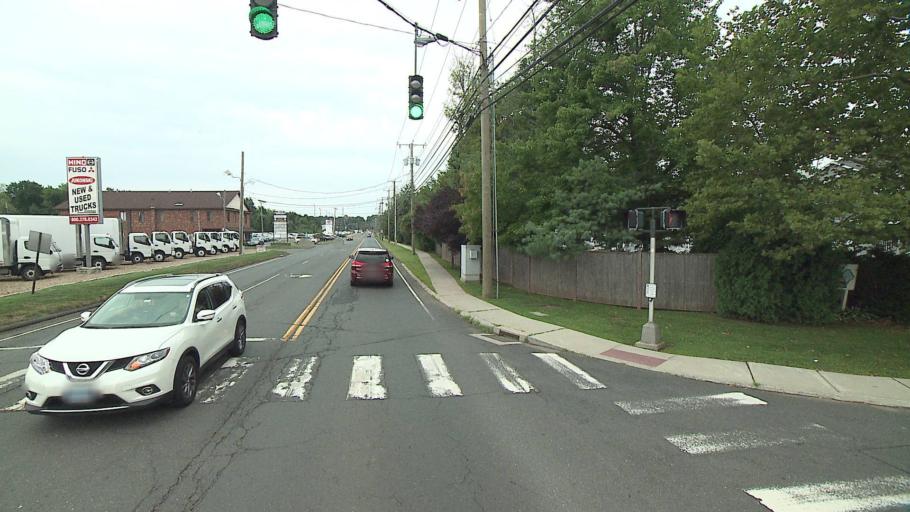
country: US
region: Connecticut
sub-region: Middlesex County
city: Middletown
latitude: 41.5779
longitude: -72.6724
